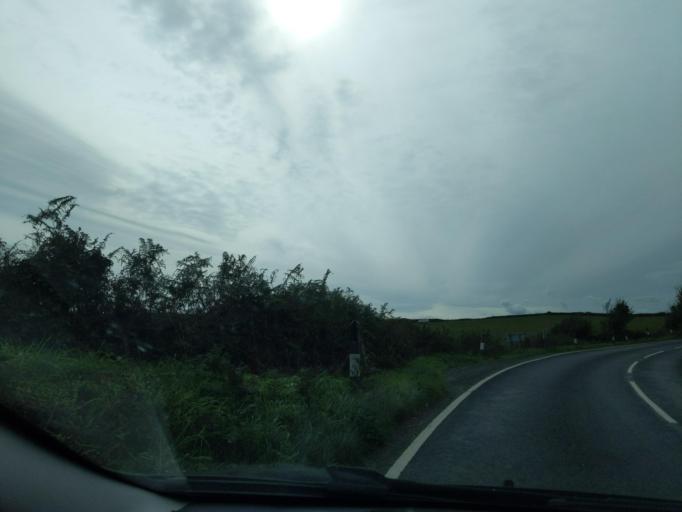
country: GB
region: England
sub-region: Cornwall
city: Mevagissey
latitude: 50.2842
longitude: -4.7861
